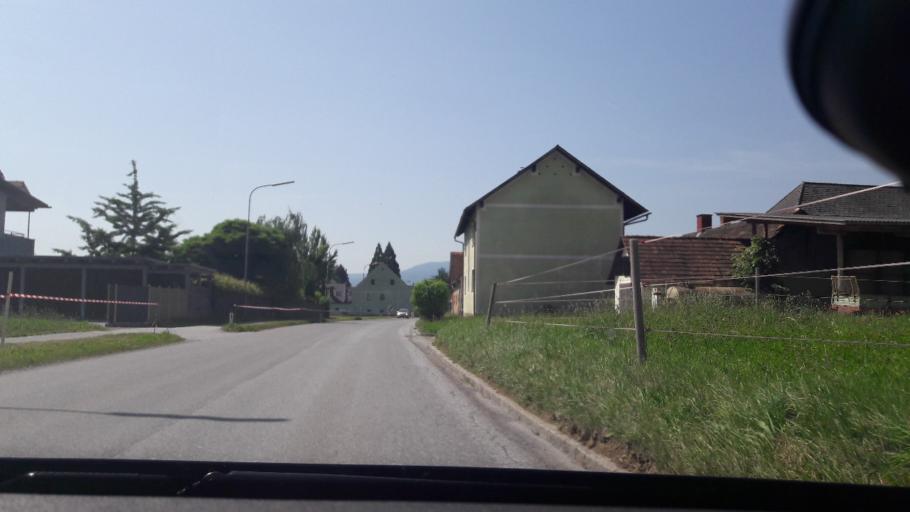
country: AT
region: Styria
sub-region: Politischer Bezirk Voitsberg
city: Kohlschwarz
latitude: 47.0857
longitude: 15.1234
